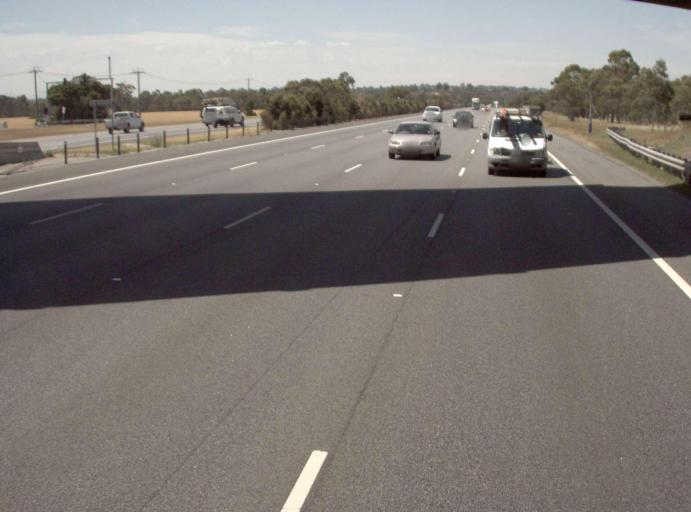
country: AU
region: Victoria
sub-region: Greater Dandenong
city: Dandenong North
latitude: -37.9600
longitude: 145.2252
